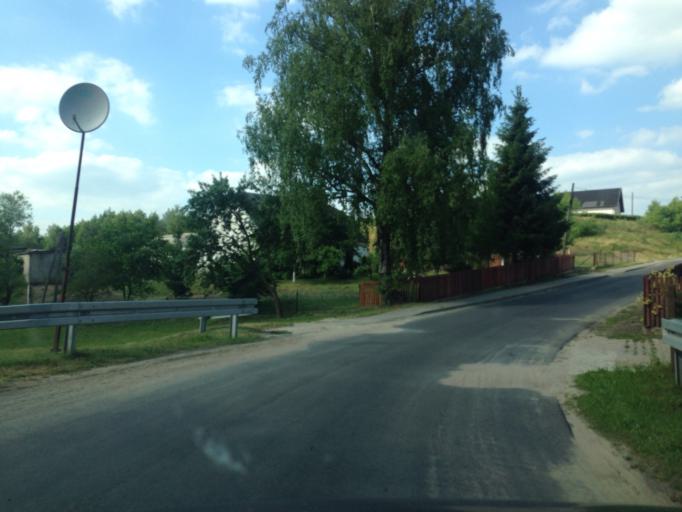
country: PL
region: Kujawsko-Pomorskie
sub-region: Powiat brodnicki
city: Bartniczka
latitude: 53.2691
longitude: 19.6437
